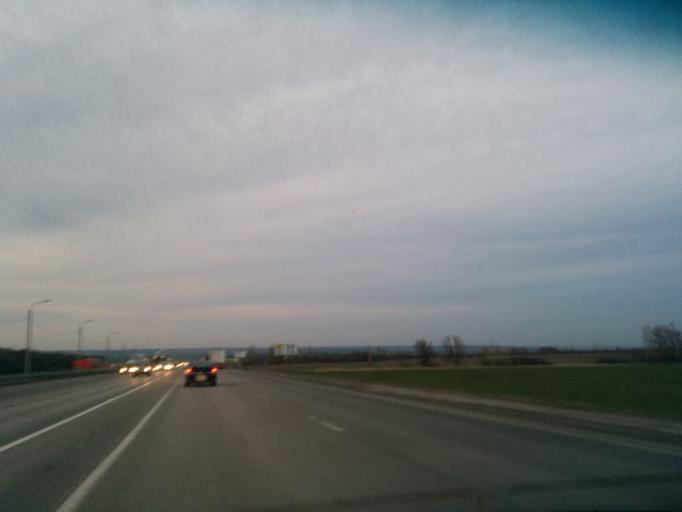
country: RU
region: Rostov
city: Grushevskaya
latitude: 47.4165
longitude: 39.9750
